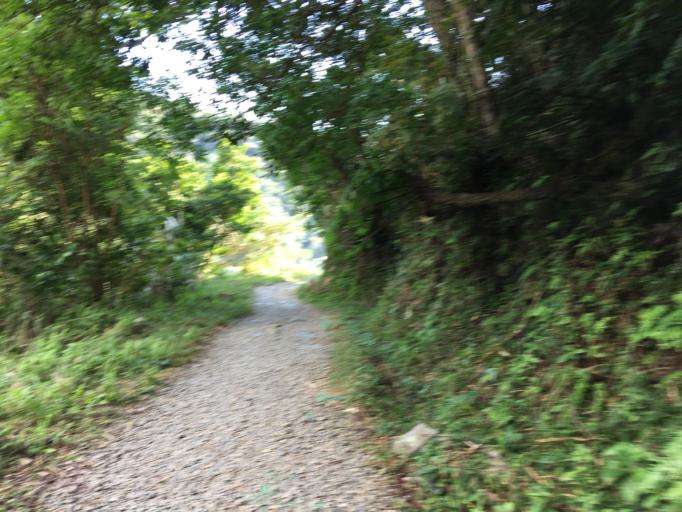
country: TW
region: Taiwan
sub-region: Yilan
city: Yilan
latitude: 24.8470
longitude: 121.7760
